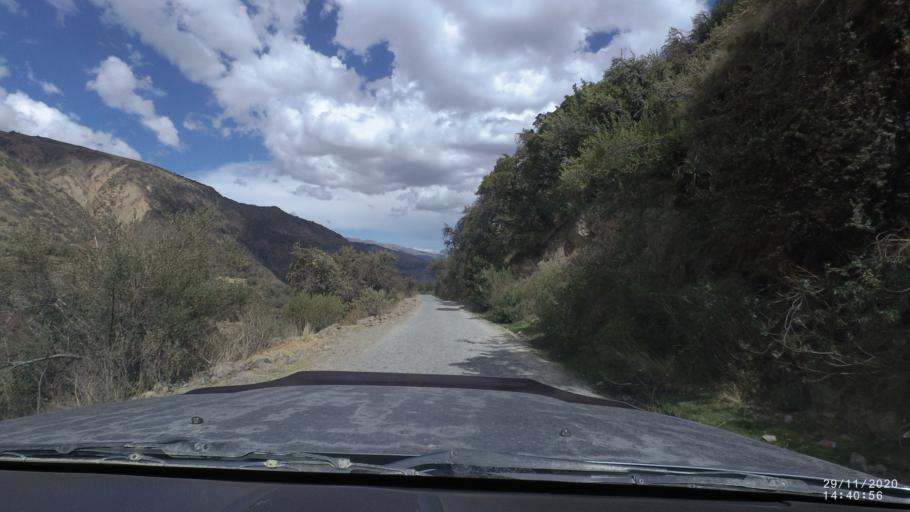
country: BO
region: Cochabamba
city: Sipe Sipe
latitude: -17.2764
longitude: -66.3283
